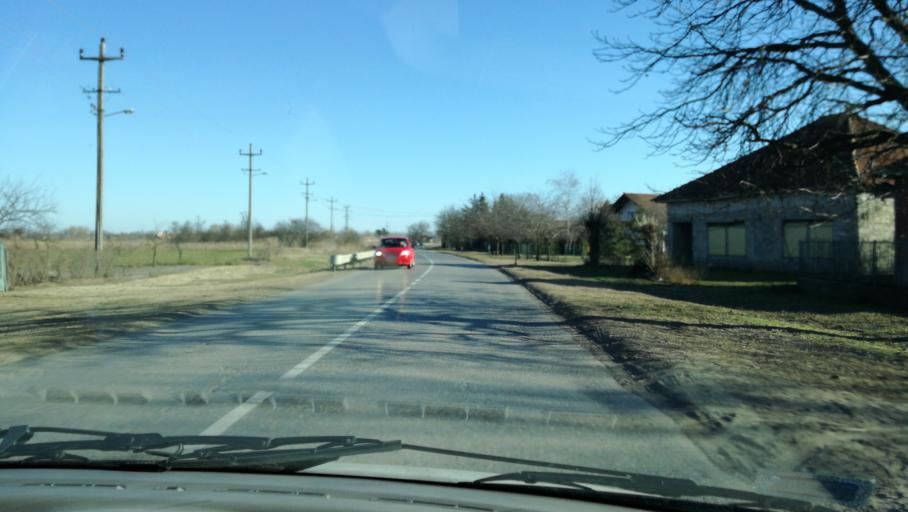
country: HU
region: Csongrad
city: Morahalom
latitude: 46.1033
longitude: 19.8689
